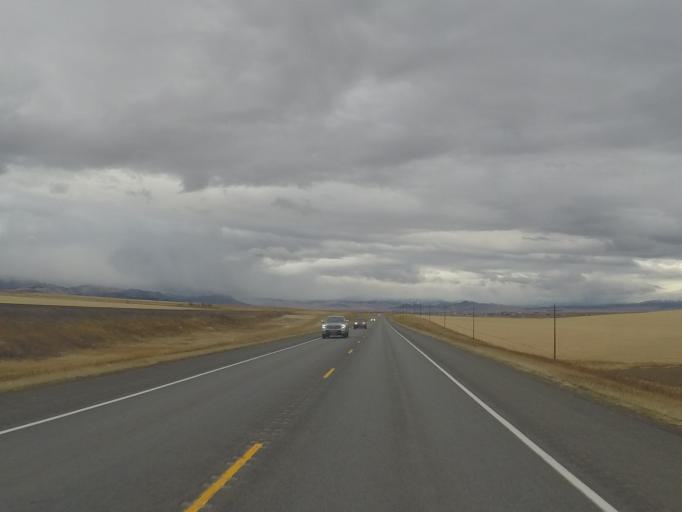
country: US
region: Montana
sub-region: Lewis and Clark County
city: East Helena
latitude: 46.5668
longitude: -111.8076
